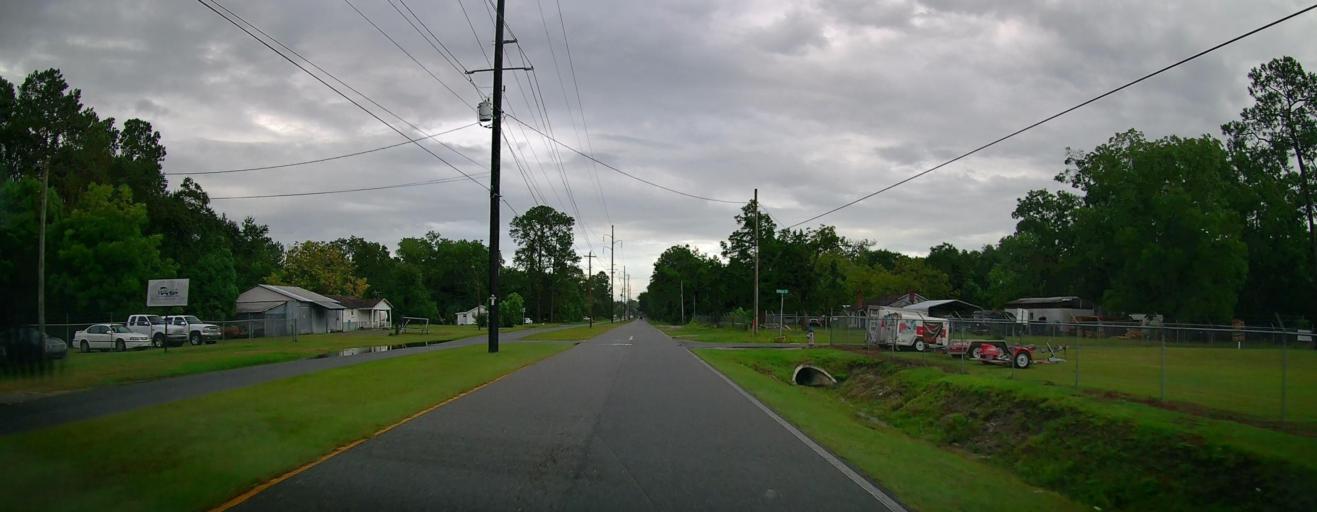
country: US
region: Georgia
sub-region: Ware County
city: Deenwood
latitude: 31.2159
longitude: -82.3882
